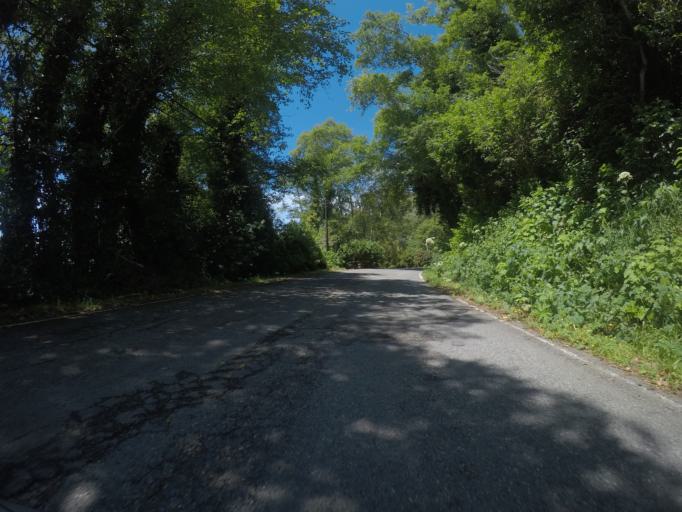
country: US
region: California
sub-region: Del Norte County
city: Bertsch-Oceanview
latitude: 41.5472
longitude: -124.0704
